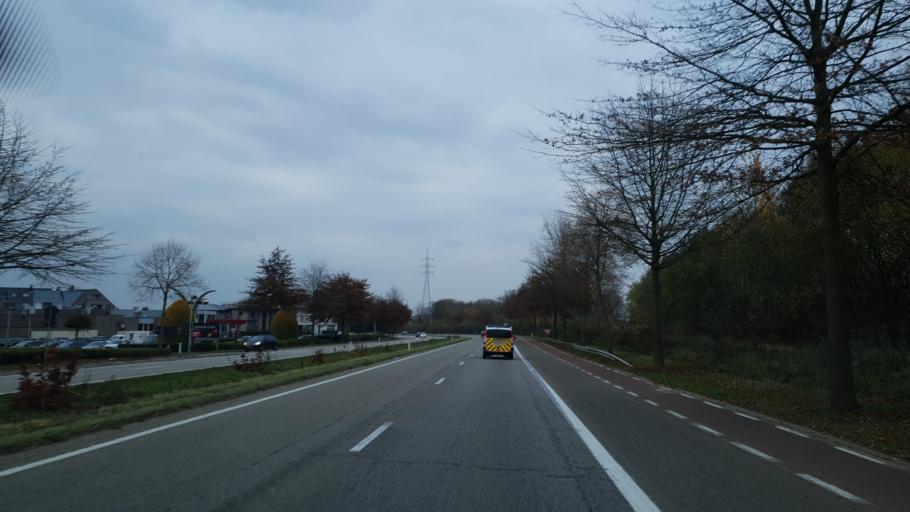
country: BE
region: Flanders
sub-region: Provincie Limburg
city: Lanaken
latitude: 50.8861
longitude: 5.6496
